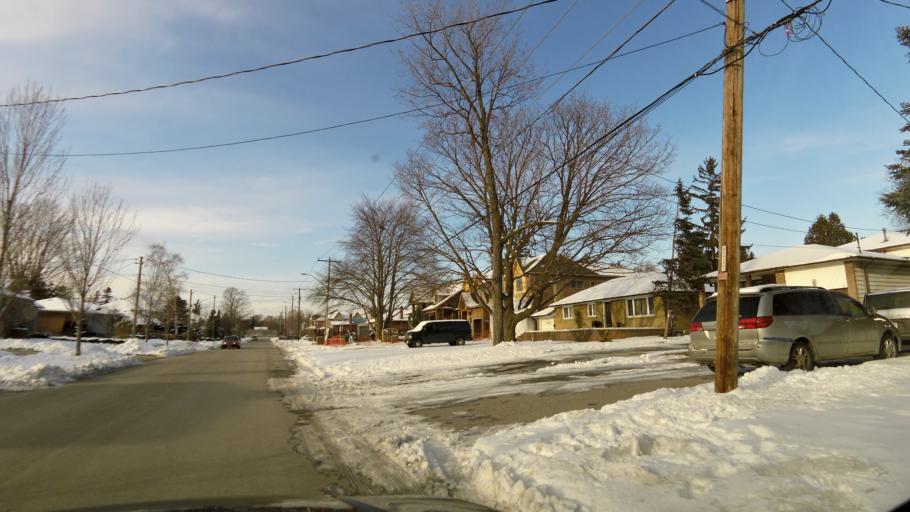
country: CA
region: Ontario
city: Etobicoke
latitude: 43.5841
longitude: -79.5775
